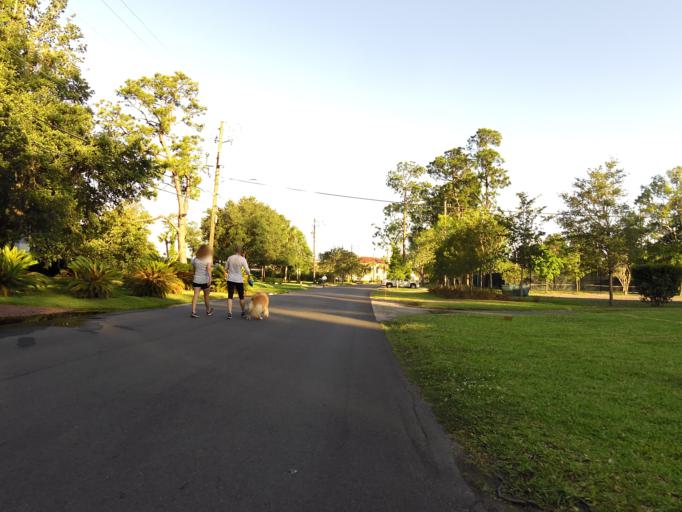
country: US
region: Florida
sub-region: Duval County
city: Jacksonville
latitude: 30.2543
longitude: -81.6909
